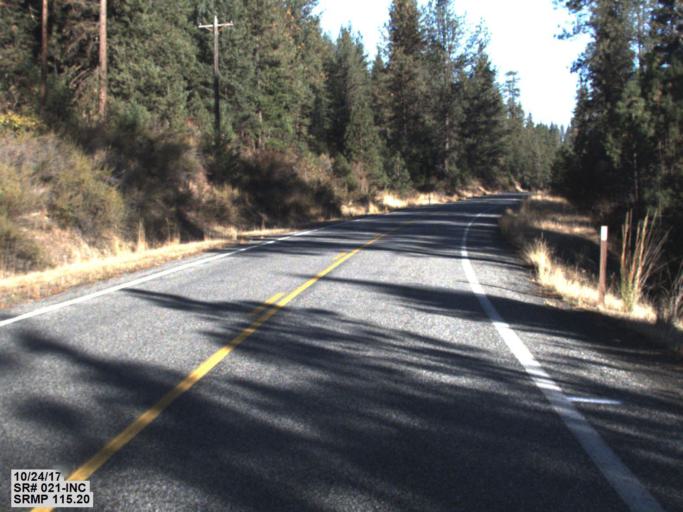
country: US
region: Washington
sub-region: Okanogan County
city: Coulee Dam
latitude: 48.0593
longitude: -118.6727
